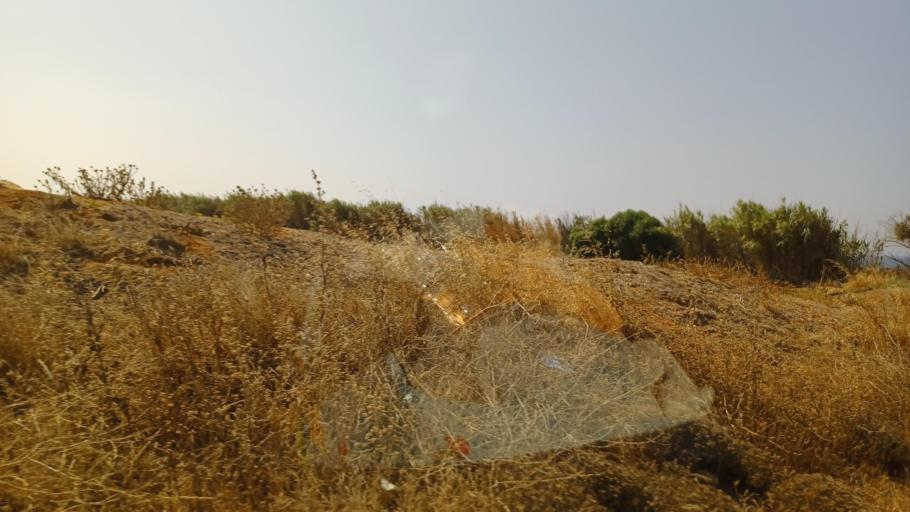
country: CY
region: Larnaka
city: Xylotymbou
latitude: 34.9753
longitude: 33.7976
